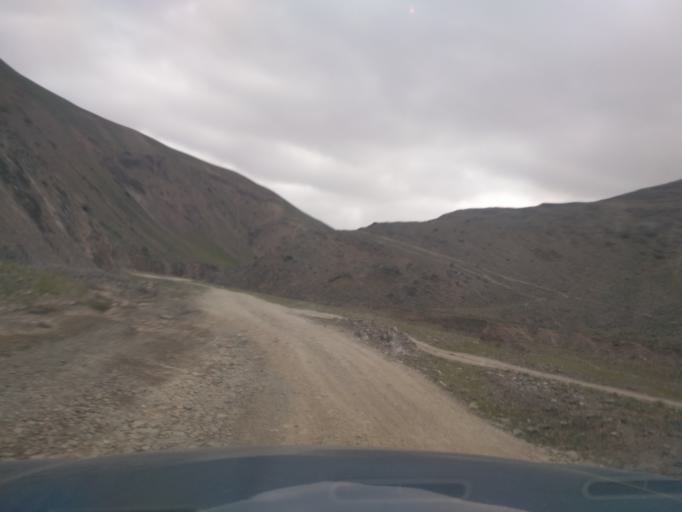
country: UZ
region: Jizzax
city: Zomin
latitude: 39.8465
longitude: 68.4002
